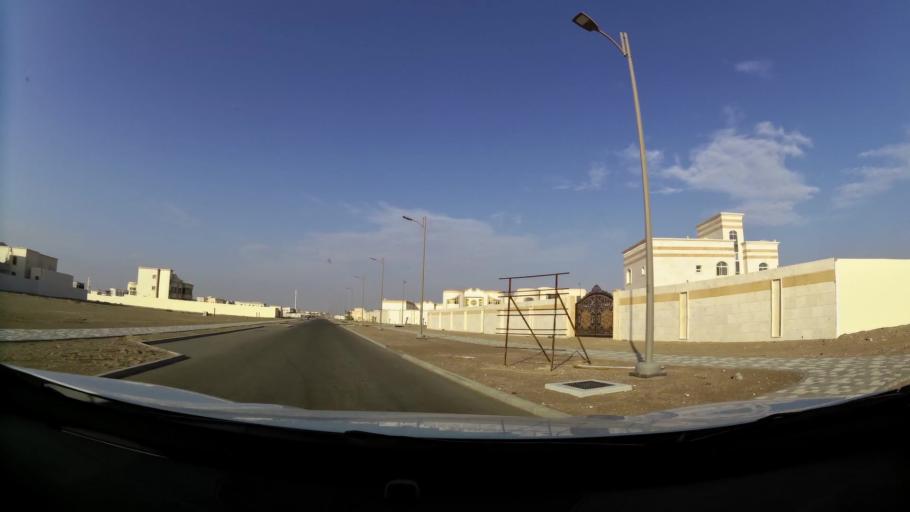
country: AE
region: Abu Dhabi
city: Al Ain
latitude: 24.1048
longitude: 55.8519
